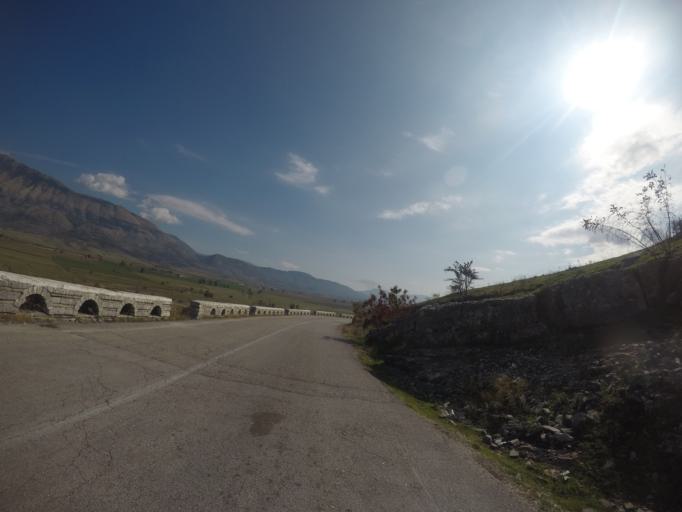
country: AL
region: Gjirokaster
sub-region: Rrethi i Gjirokastres
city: Libohove
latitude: 39.9416
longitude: 20.2608
